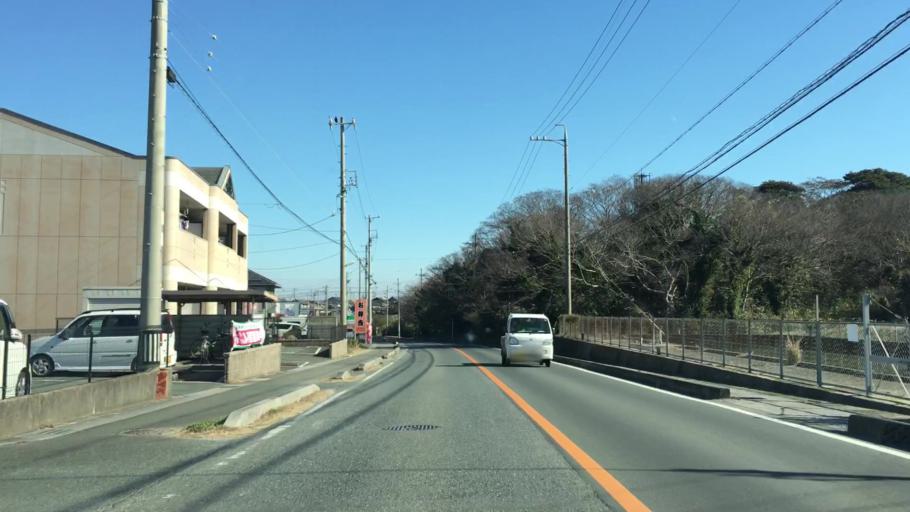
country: JP
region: Aichi
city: Tahara
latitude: 34.6925
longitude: 137.2593
